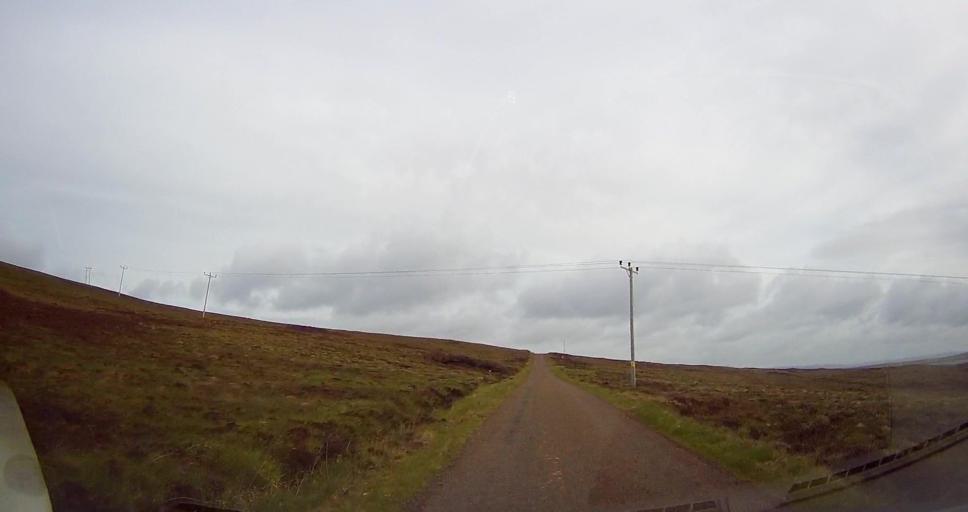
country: GB
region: Scotland
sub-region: Orkney Islands
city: Stromness
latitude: 58.8624
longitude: -3.2225
